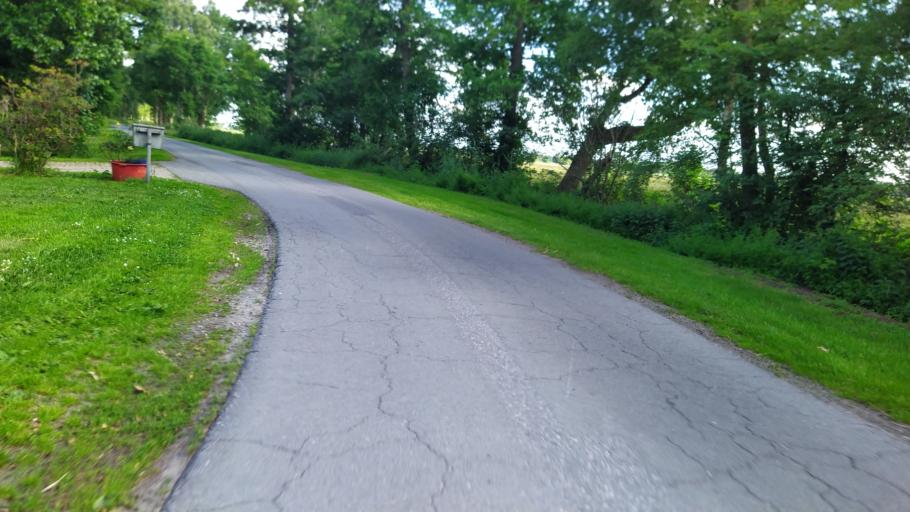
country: DE
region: Lower Saxony
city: Steinau
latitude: 53.6505
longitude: 8.9022
